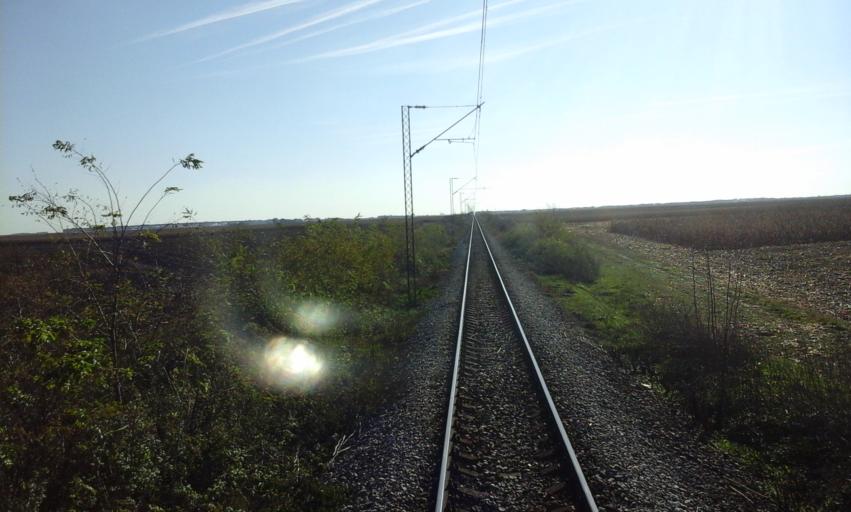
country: RS
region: Autonomna Pokrajina Vojvodina
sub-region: Severnobacki Okrug
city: Backa Topola
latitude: 45.9094
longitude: 19.6638
